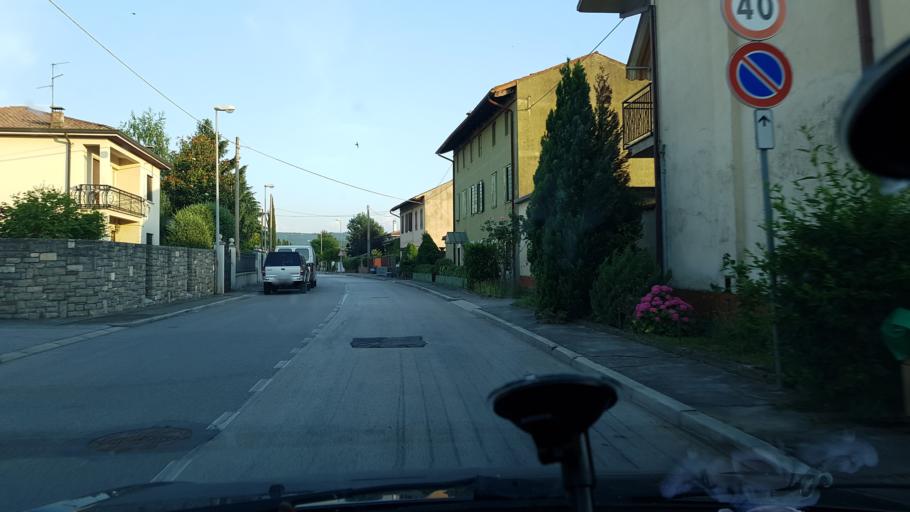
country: IT
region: Friuli Venezia Giulia
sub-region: Provincia di Gorizia
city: San Lorenzo Isontino
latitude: 45.9274
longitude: 13.5275
